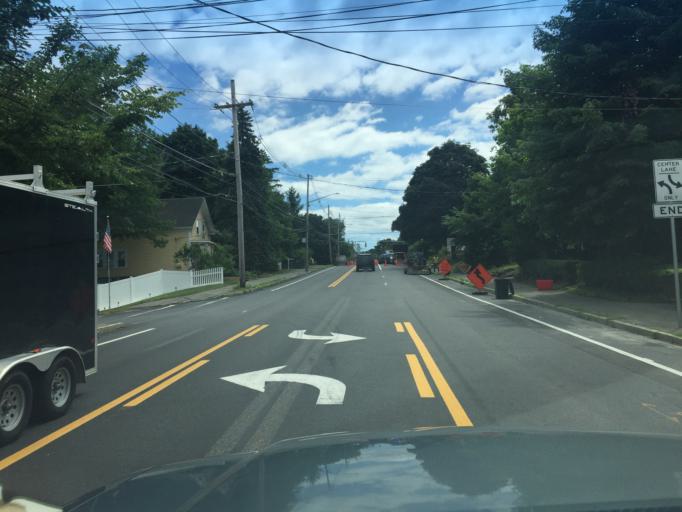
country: US
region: Massachusetts
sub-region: Middlesex County
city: Reading
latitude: 42.5120
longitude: -71.1040
